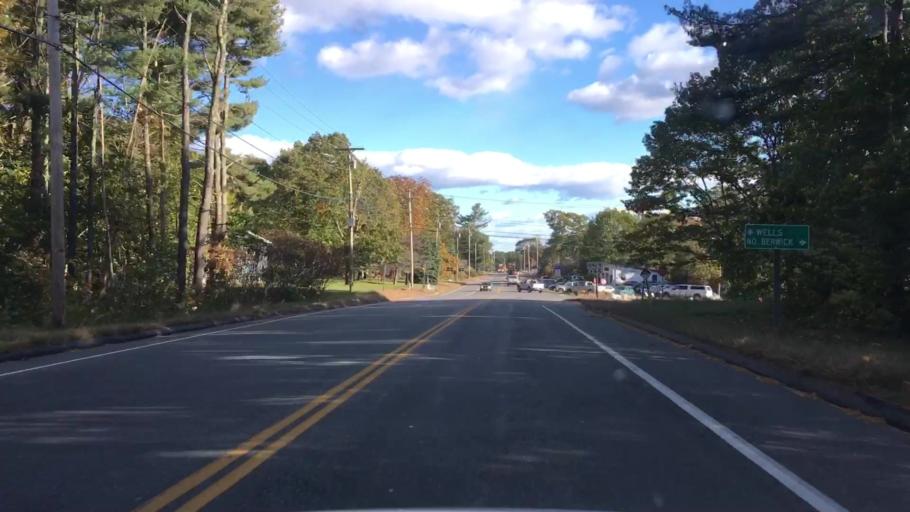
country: US
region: Maine
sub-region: York County
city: Wells Beach Station
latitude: 43.3290
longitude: -70.6212
